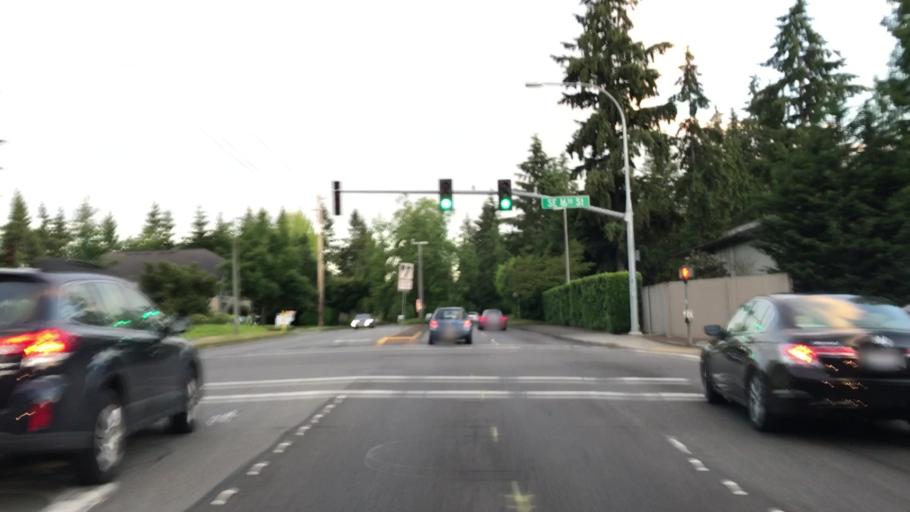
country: US
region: Washington
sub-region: King County
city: Eastgate
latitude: 47.5965
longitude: -122.1427
